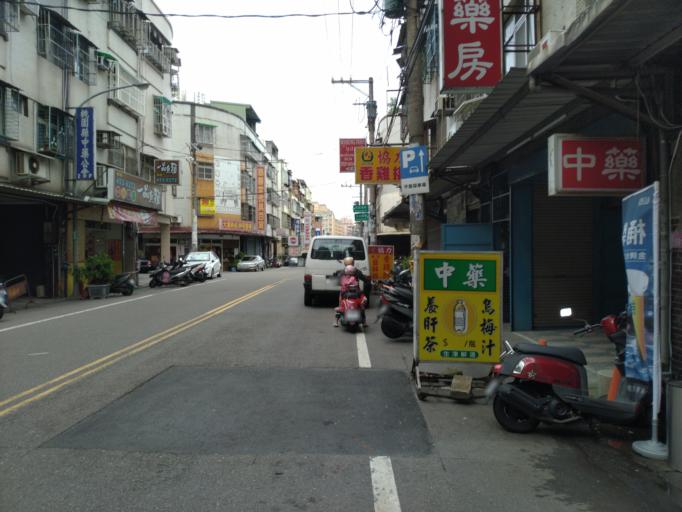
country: TW
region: Taiwan
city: Taoyuan City
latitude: 24.9787
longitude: 121.2511
